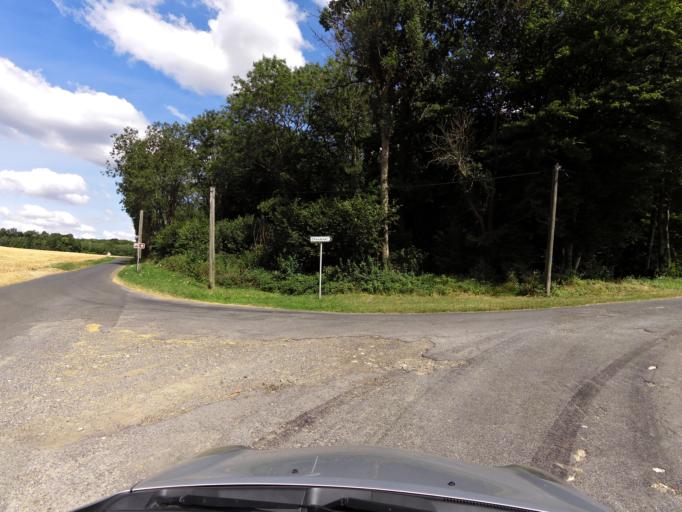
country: FR
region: Picardie
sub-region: Departement de l'Aisne
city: Bruyeres-et-Montberault
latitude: 49.4992
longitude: 3.6446
